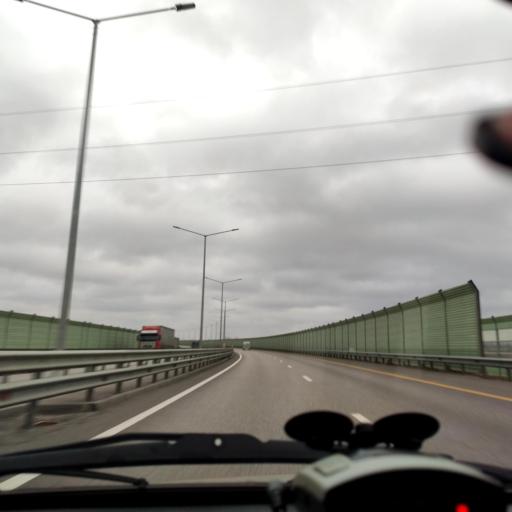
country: RU
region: Voronezj
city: Novaya Usman'
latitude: 51.6064
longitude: 39.3252
